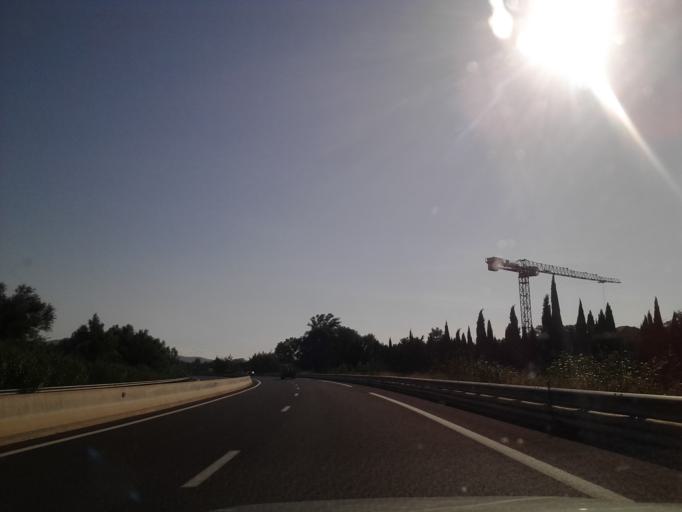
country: FR
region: Languedoc-Roussillon
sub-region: Departement des Pyrenees-Orientales
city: Ille-sur-Tet
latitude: 42.6752
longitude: 2.6224
